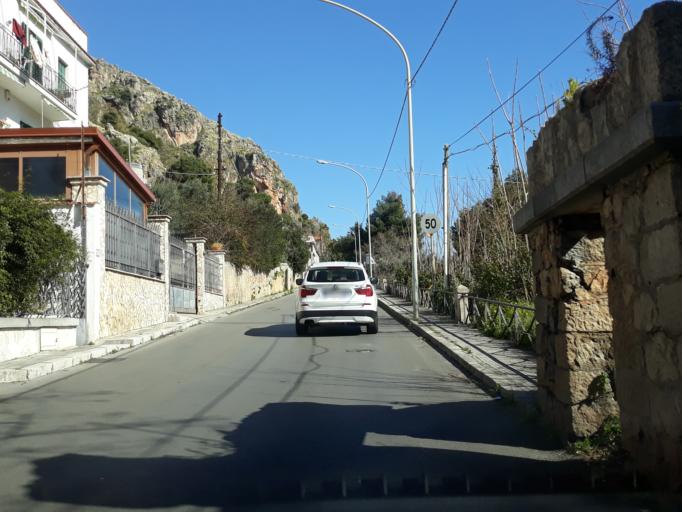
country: IT
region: Sicily
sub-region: Palermo
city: Monreale
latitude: 38.0923
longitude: 13.3051
